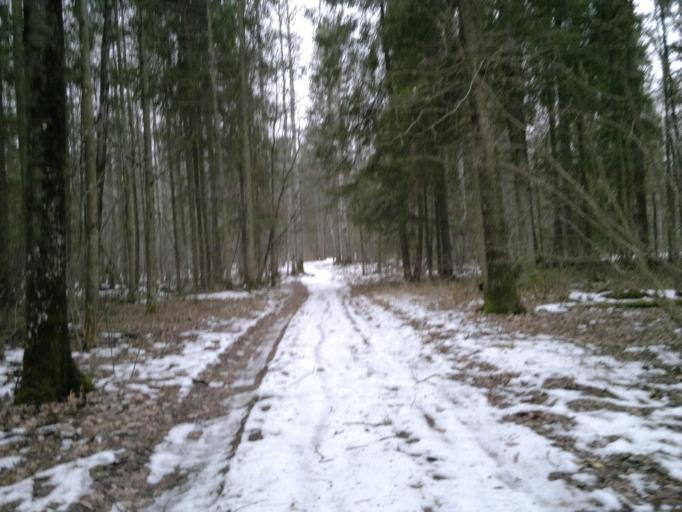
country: RU
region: Mariy-El
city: Yoshkar-Ola
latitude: 56.6039
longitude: 47.9621
